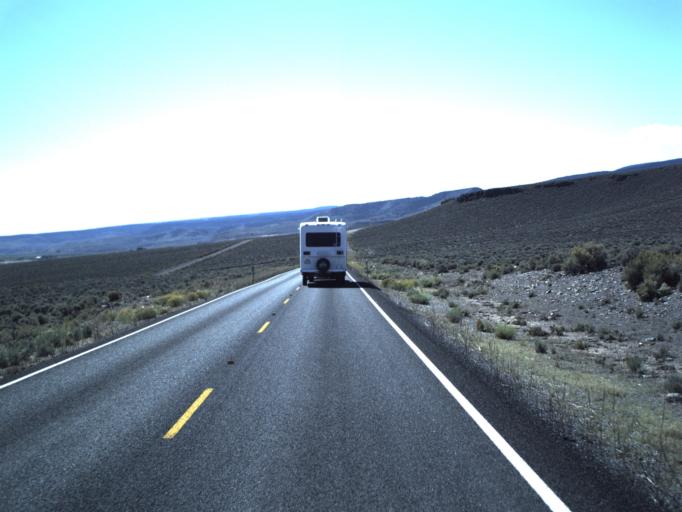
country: US
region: Utah
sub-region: Piute County
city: Junction
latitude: 38.1903
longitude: -112.0125
